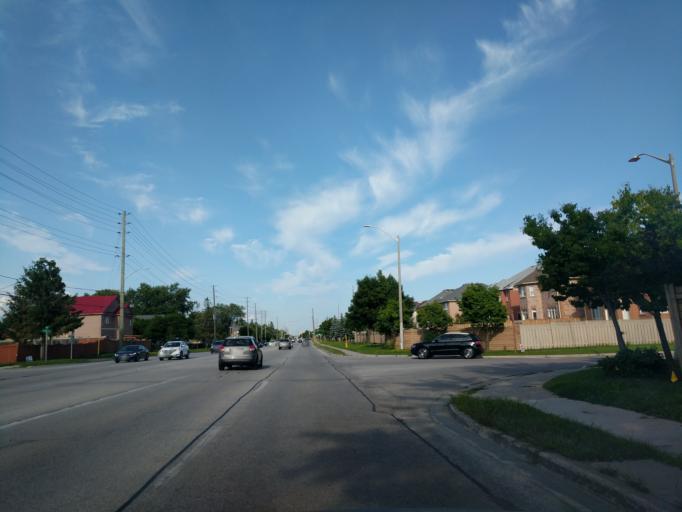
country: CA
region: Ontario
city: Markham
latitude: 43.8479
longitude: -79.2851
